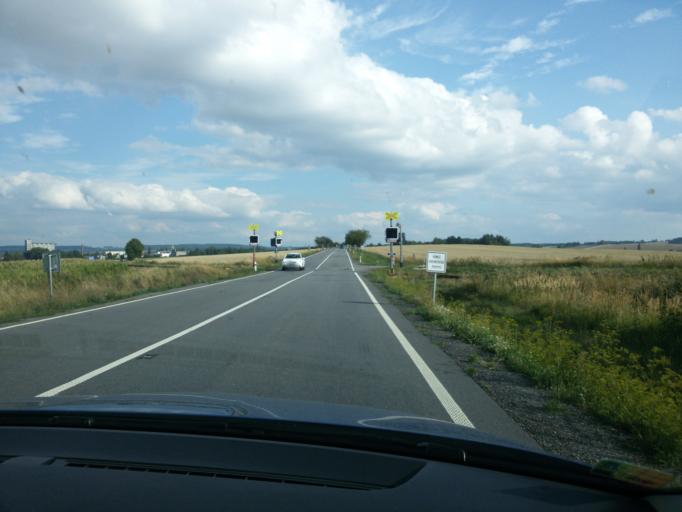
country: CZ
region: Pardubicky
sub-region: Okres Svitavy
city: Policka
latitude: 49.7222
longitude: 16.2361
